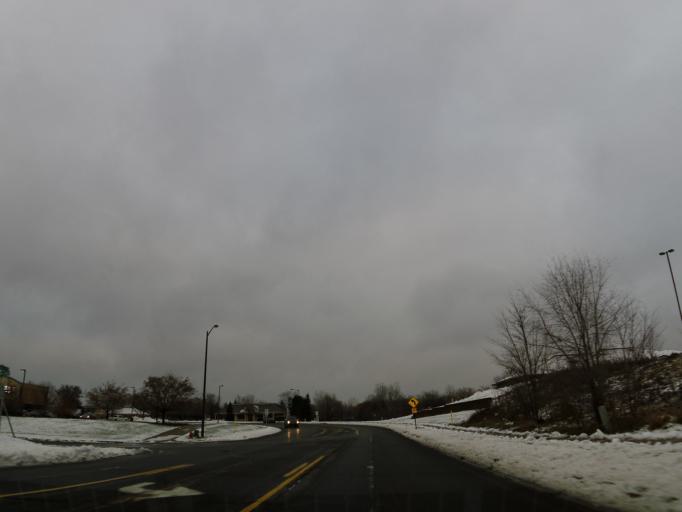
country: US
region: Minnesota
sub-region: Dakota County
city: Burnsville
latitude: 44.7122
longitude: -93.2816
